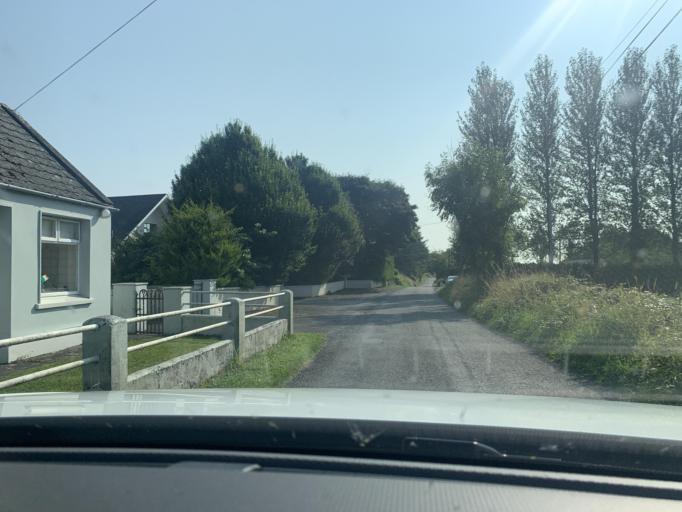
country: IE
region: Connaught
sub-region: Maigh Eo
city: Ballyhaunis
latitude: 53.8125
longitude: -8.7505
